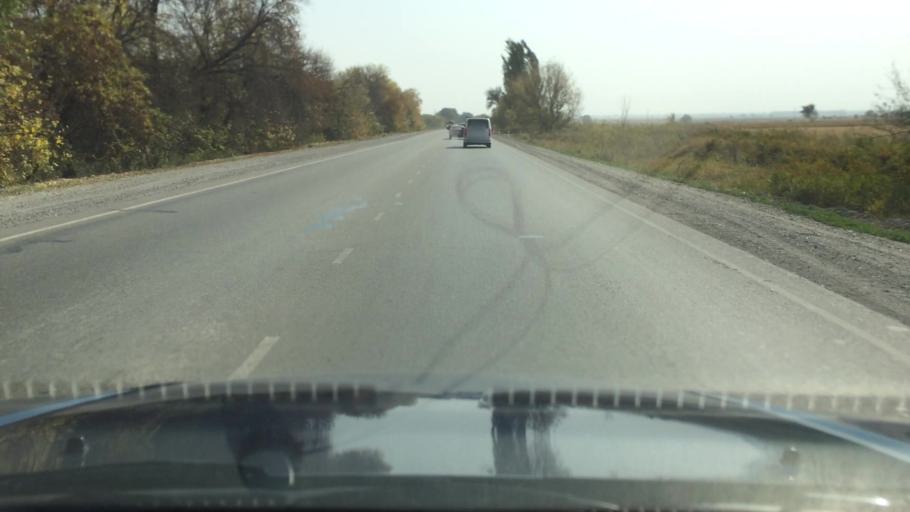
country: KG
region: Chuy
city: Lebedinovka
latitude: 42.9273
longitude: 74.6971
